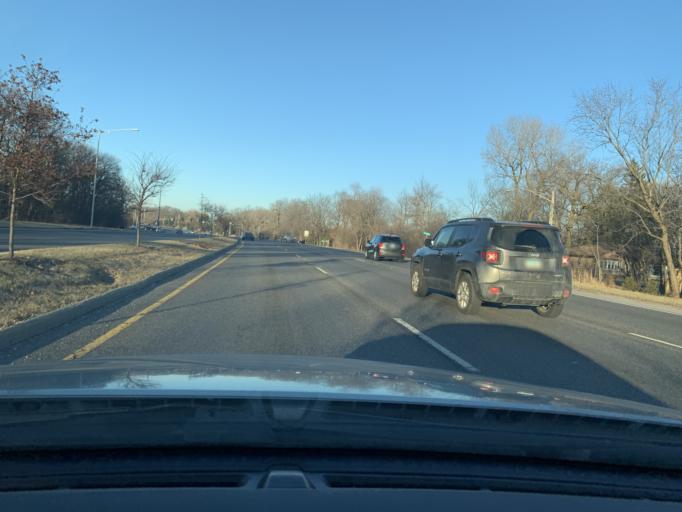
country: US
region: Illinois
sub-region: DuPage County
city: Bensenville
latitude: 41.9433
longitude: -87.9608
